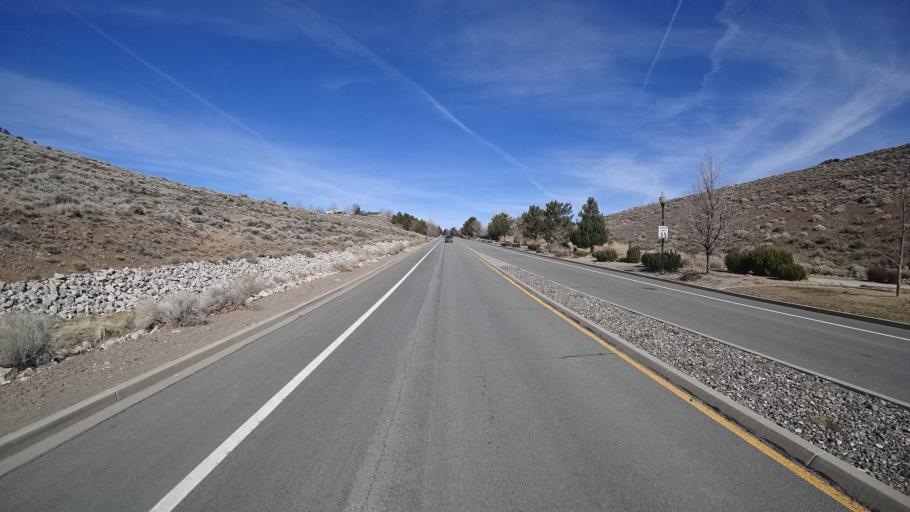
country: US
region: Nevada
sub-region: Washoe County
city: Sparks
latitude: 39.5738
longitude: -119.6955
